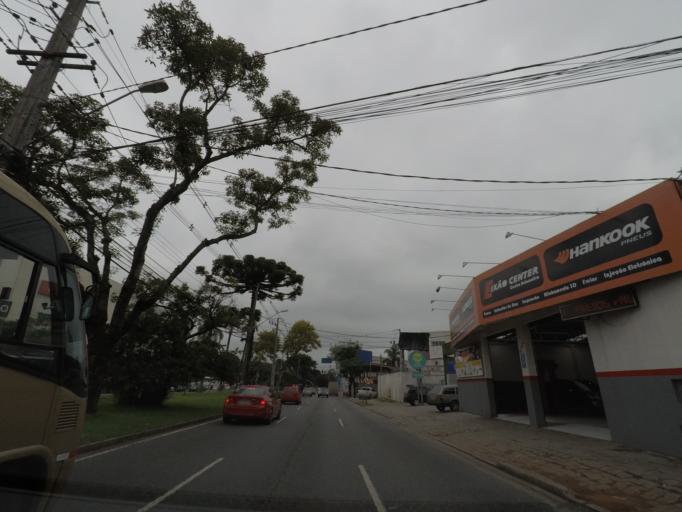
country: BR
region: Parana
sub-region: Curitiba
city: Curitiba
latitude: -25.4768
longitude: -49.2913
